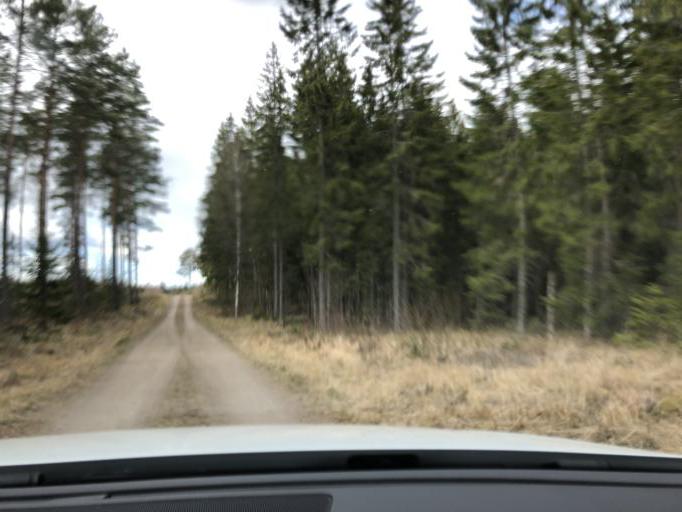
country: SE
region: Gaevleborg
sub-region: Gavle Kommun
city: Hedesunda
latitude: 60.3374
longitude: 17.1100
